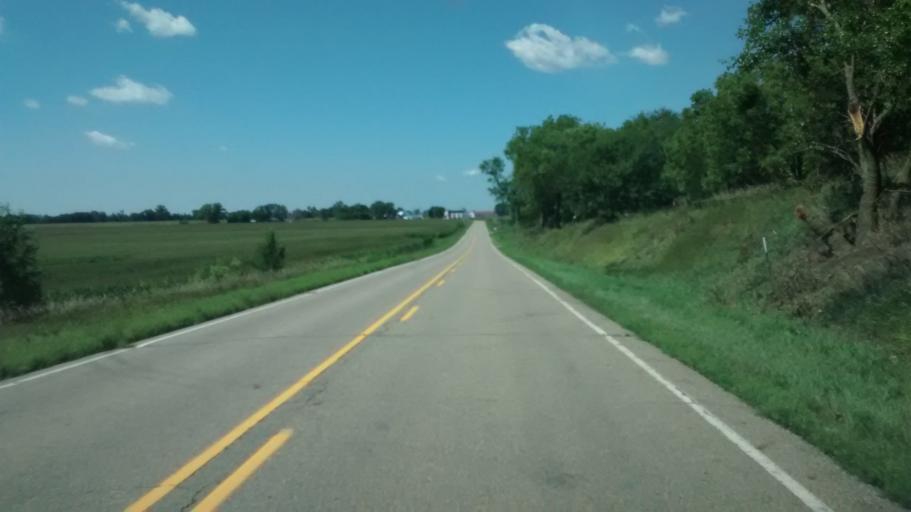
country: US
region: Iowa
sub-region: Woodbury County
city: Moville
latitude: 42.2689
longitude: -96.0674
